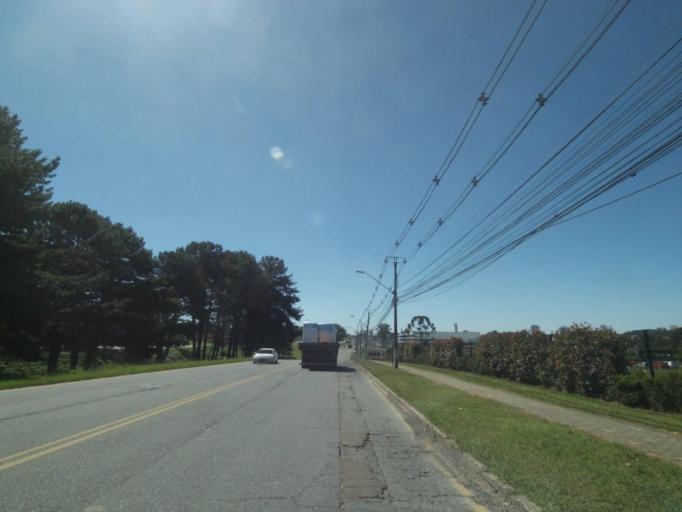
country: BR
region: Parana
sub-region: Curitiba
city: Curitiba
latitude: -25.4683
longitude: -49.3548
